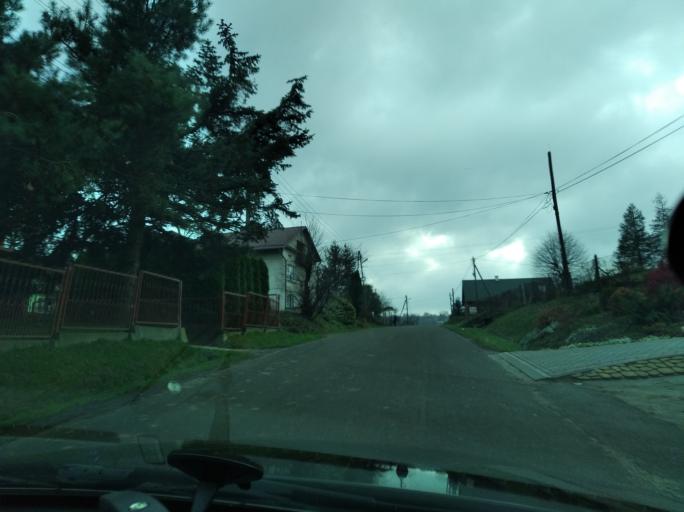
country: PL
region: Subcarpathian Voivodeship
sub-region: Powiat przeworski
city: Sietesz
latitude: 49.9838
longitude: 22.3455
